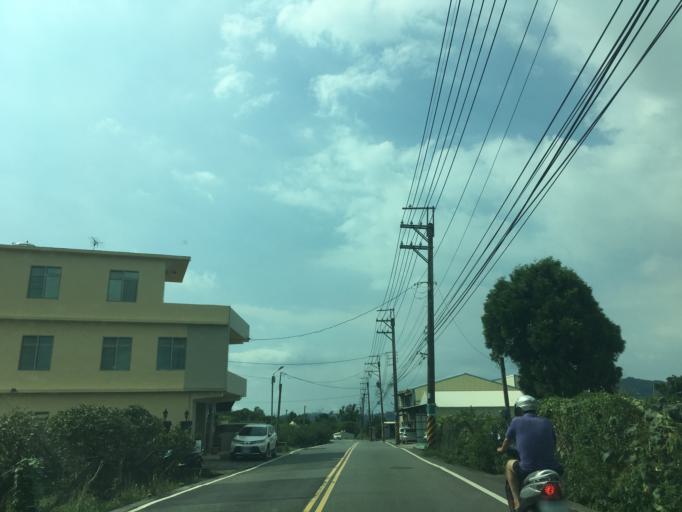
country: TW
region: Taiwan
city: Fengyuan
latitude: 24.2551
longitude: 120.8144
